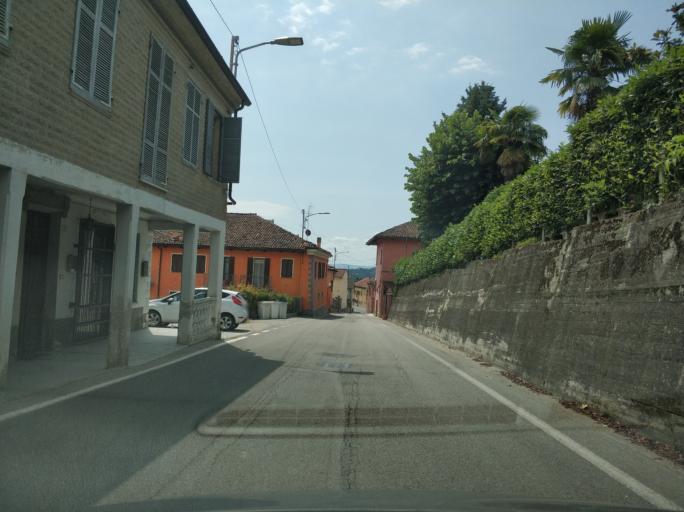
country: IT
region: Piedmont
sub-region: Provincia di Cuneo
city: Santo Stefano Roero
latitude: 44.7882
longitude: 7.9418
